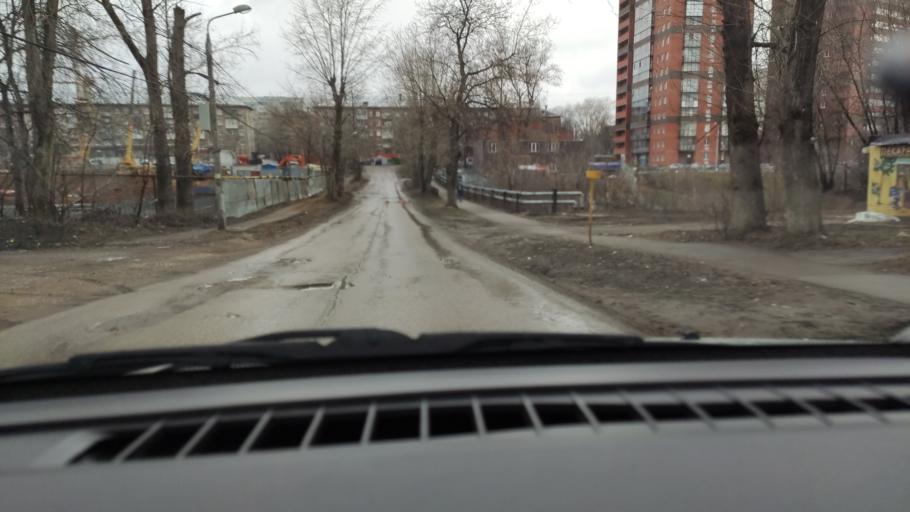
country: RU
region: Perm
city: Perm
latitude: 58.1077
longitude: 56.3074
